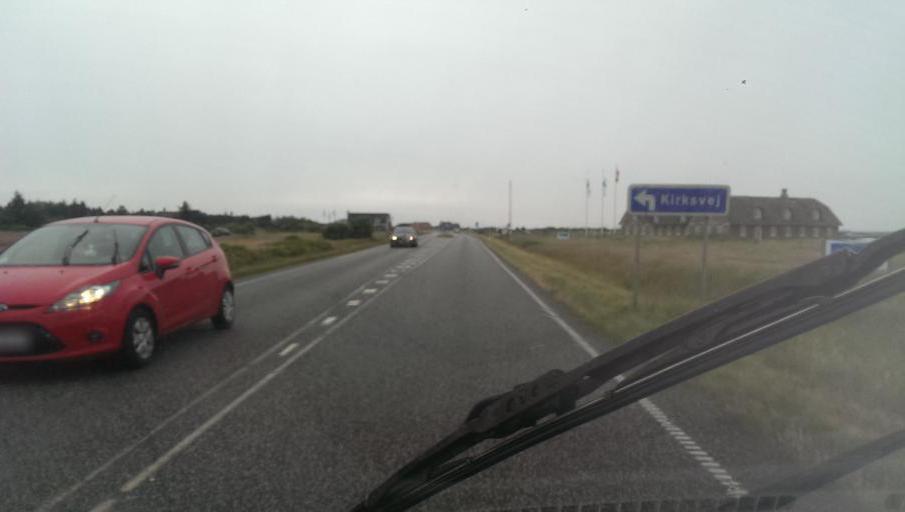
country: DK
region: Central Jutland
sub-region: Ringkobing-Skjern Kommune
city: Hvide Sande
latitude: 55.8615
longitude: 8.1807
